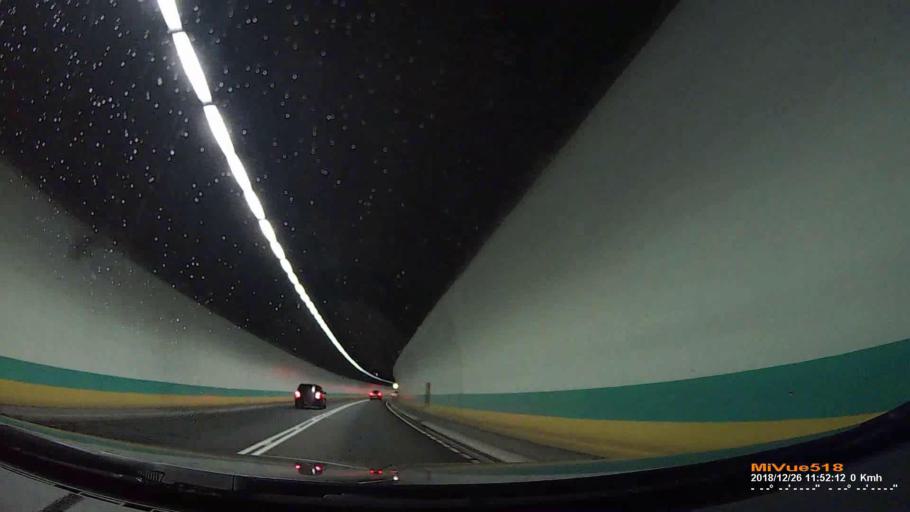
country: TW
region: Taiwan
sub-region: Keelung
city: Keelung
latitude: 24.9687
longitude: 121.6828
